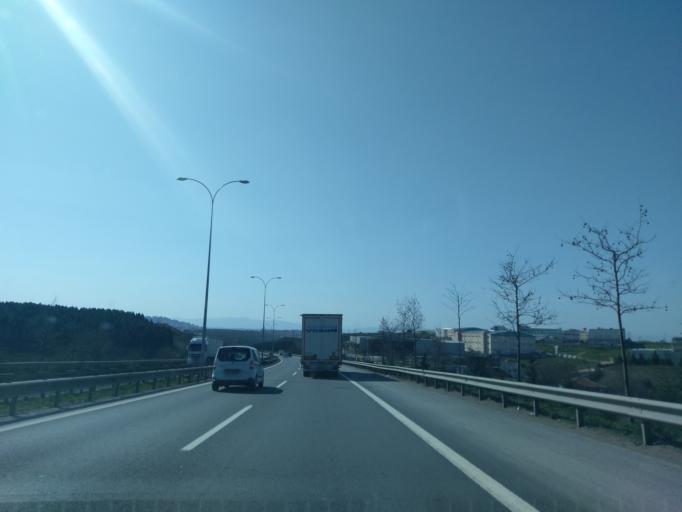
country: TR
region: Kocaeli
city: Balcik
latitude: 40.8530
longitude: 29.3749
